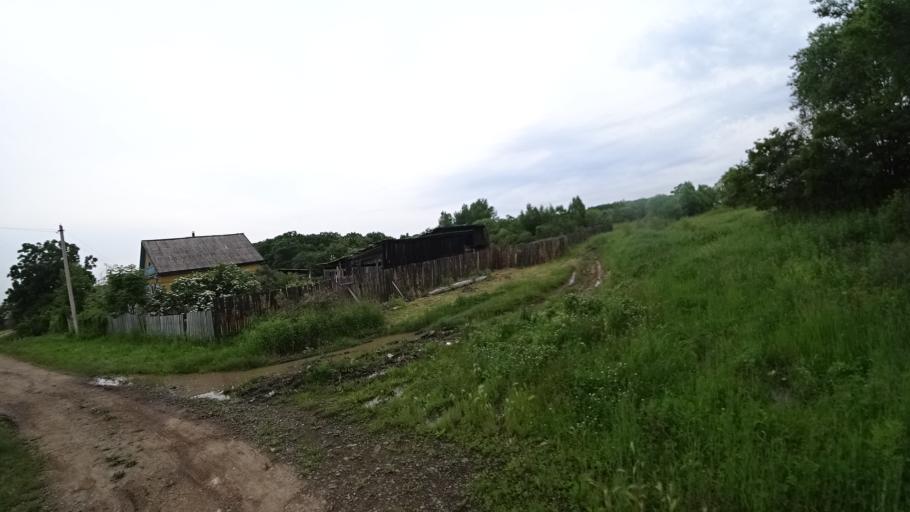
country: RU
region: Primorskiy
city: Novosysoyevka
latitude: 44.2225
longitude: 133.3539
